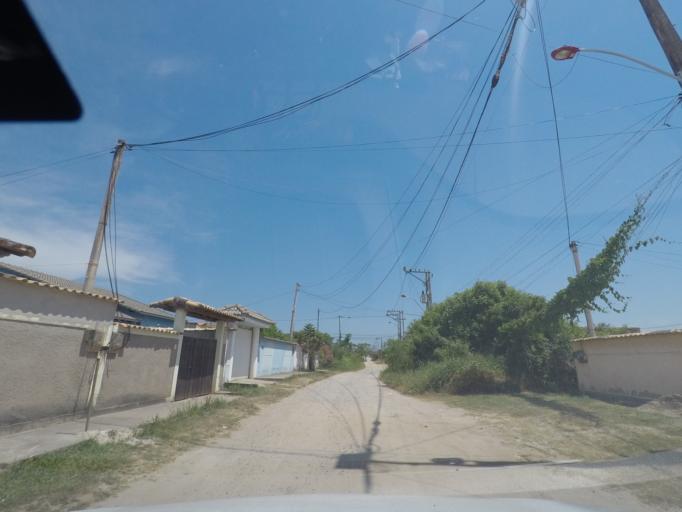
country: BR
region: Rio de Janeiro
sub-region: Marica
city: Marica
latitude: -22.9613
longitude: -42.9540
